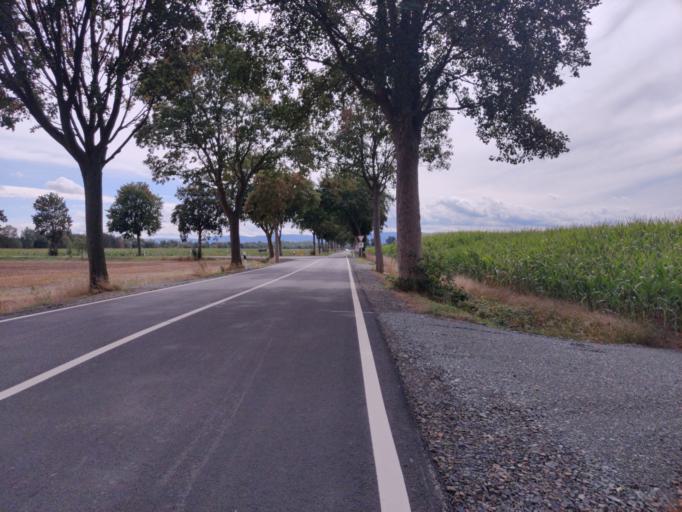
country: DE
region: Lower Saxony
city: Liebenburg
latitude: 52.0069
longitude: 10.3686
